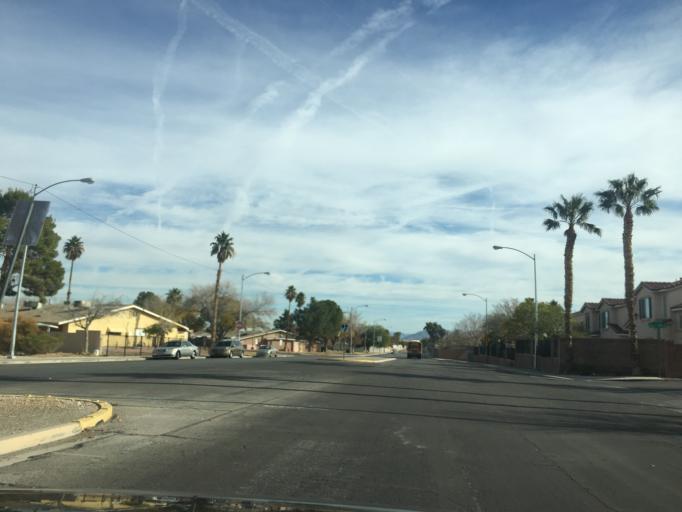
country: US
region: Nevada
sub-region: Clark County
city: Enterprise
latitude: 36.0173
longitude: -115.1702
